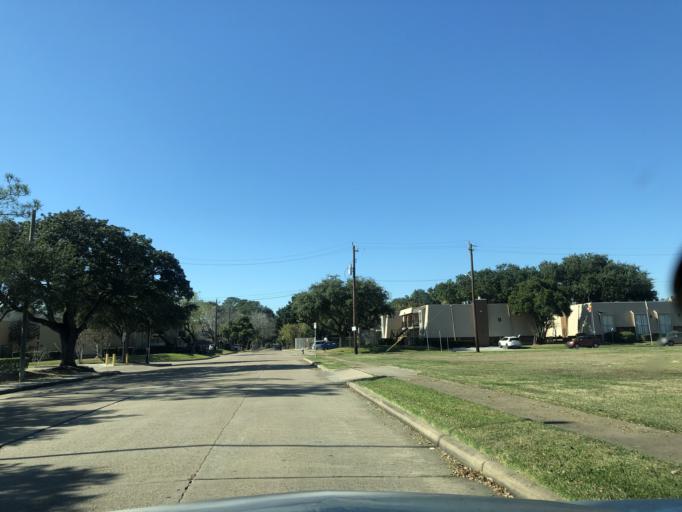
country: US
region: Texas
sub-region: Harris County
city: Bellaire
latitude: 29.6752
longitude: -95.4953
